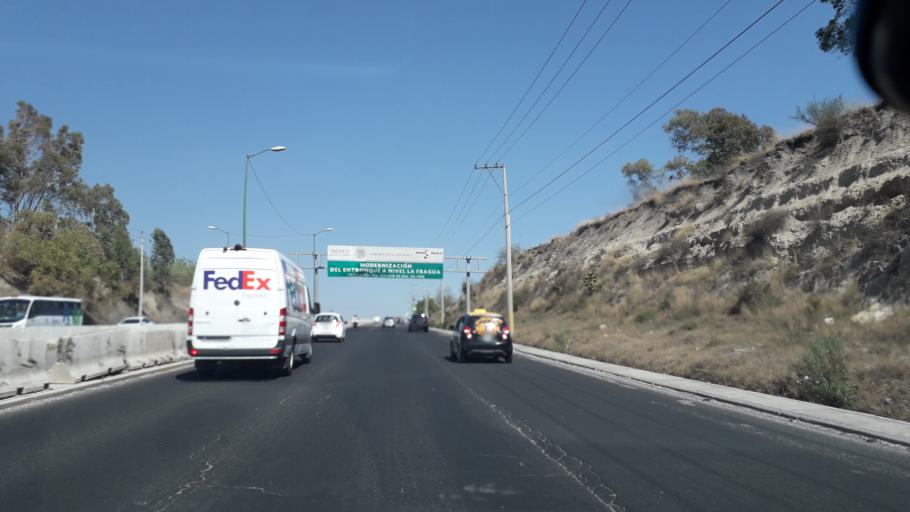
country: MX
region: Puebla
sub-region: Puebla
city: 18 de Marzo
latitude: 18.9723
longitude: -98.2062
